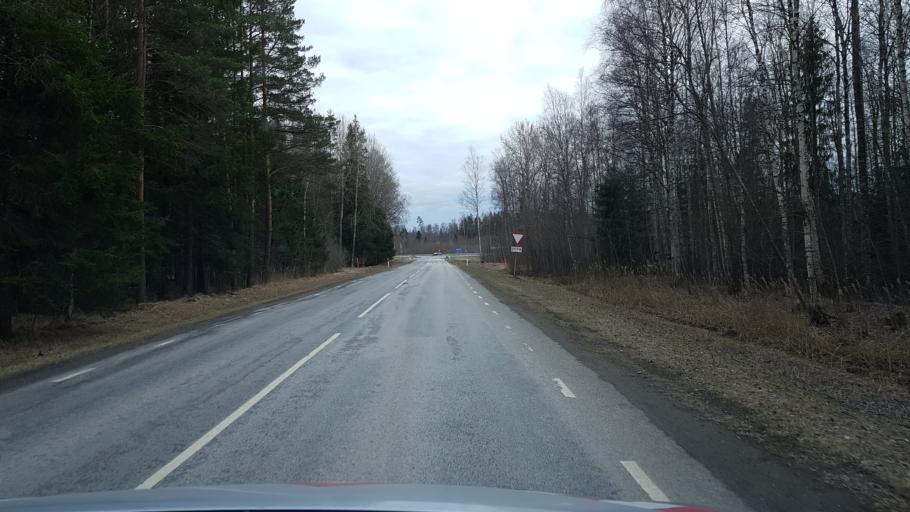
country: EE
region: Ida-Virumaa
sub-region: Toila vald
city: Toila
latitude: 59.3770
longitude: 27.5082
